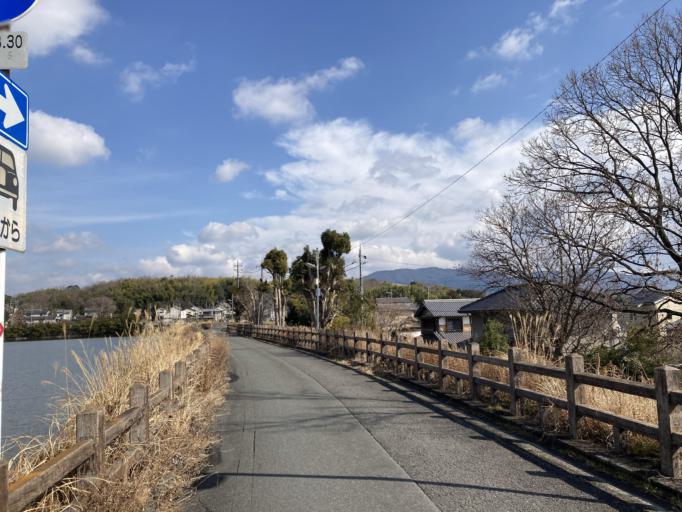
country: JP
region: Nara
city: Nara-shi
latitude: 34.6959
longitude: 135.8083
